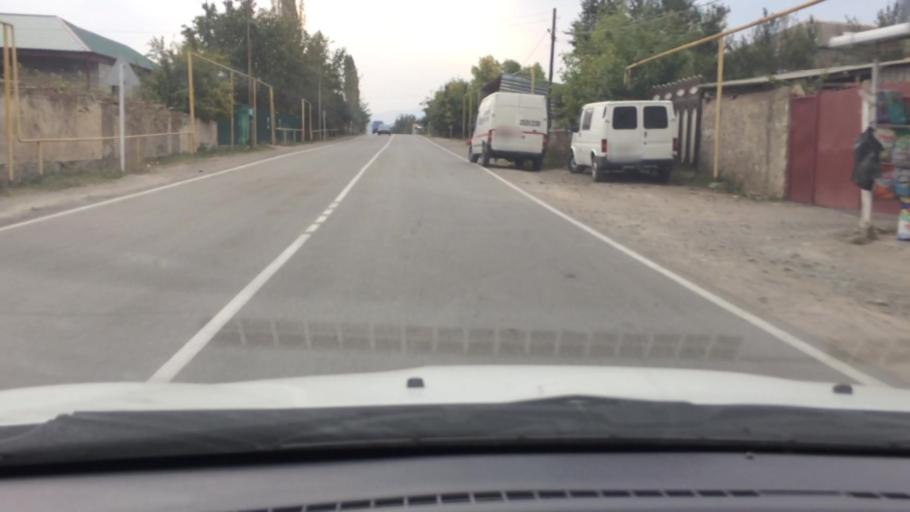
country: AM
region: Tavush
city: Bagratashen
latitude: 41.2373
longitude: 44.8043
